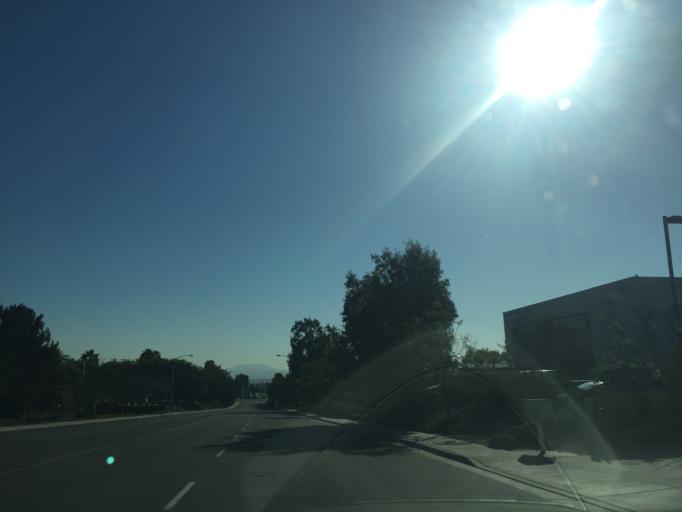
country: MX
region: Baja California
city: Tijuana
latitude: 32.5595
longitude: -116.9321
